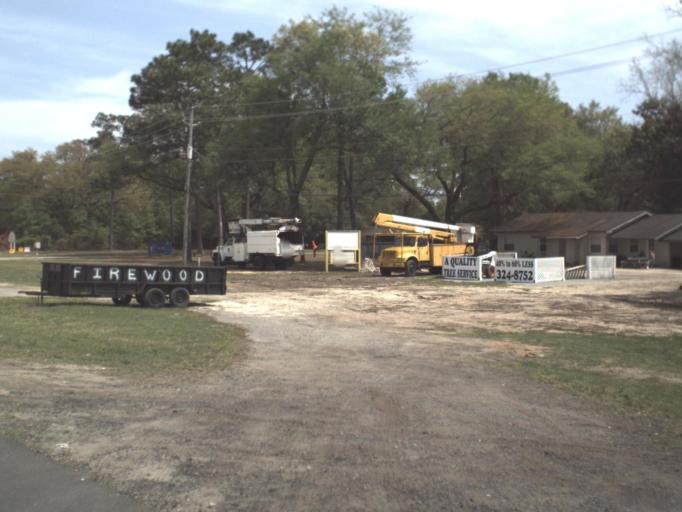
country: US
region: Florida
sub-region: Escambia County
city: Ensley
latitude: 30.5342
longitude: -87.3106
